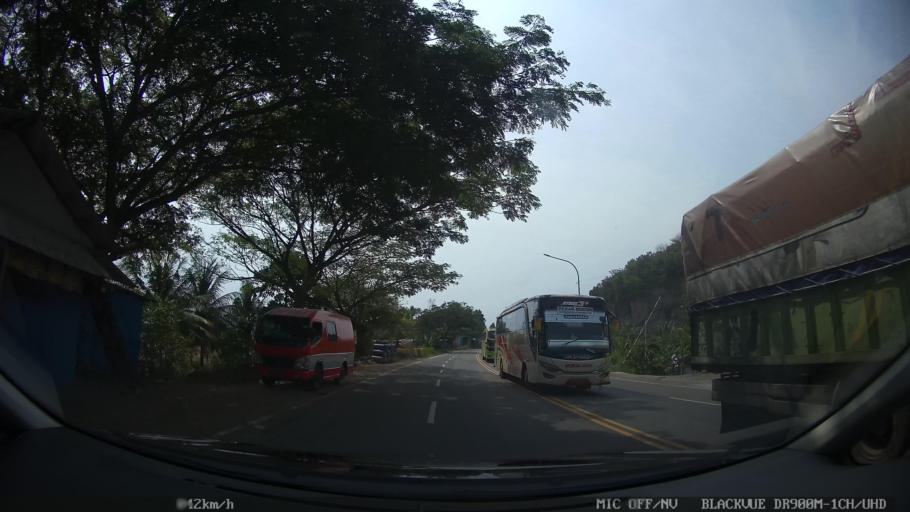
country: ID
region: Banten
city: Curug
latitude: -5.9547
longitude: 106.0027
